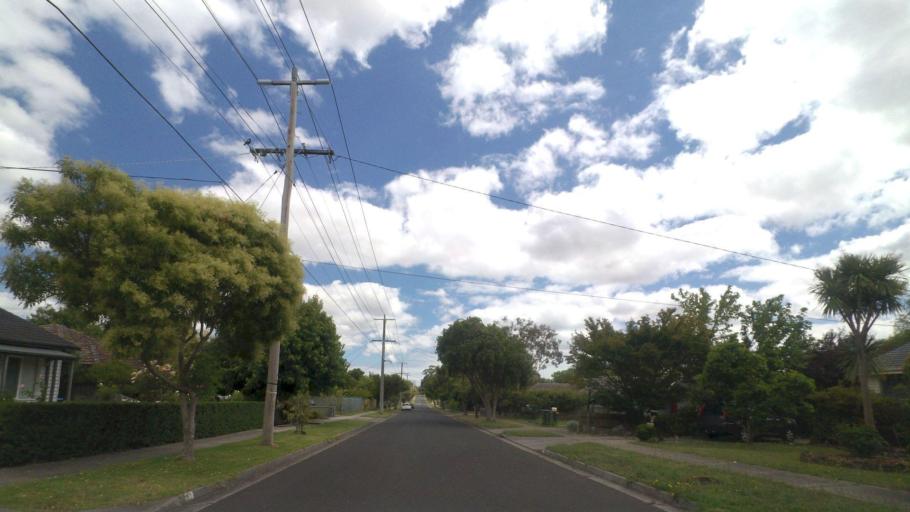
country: AU
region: Victoria
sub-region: Knox
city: Bayswater
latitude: -37.8625
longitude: 145.2616
